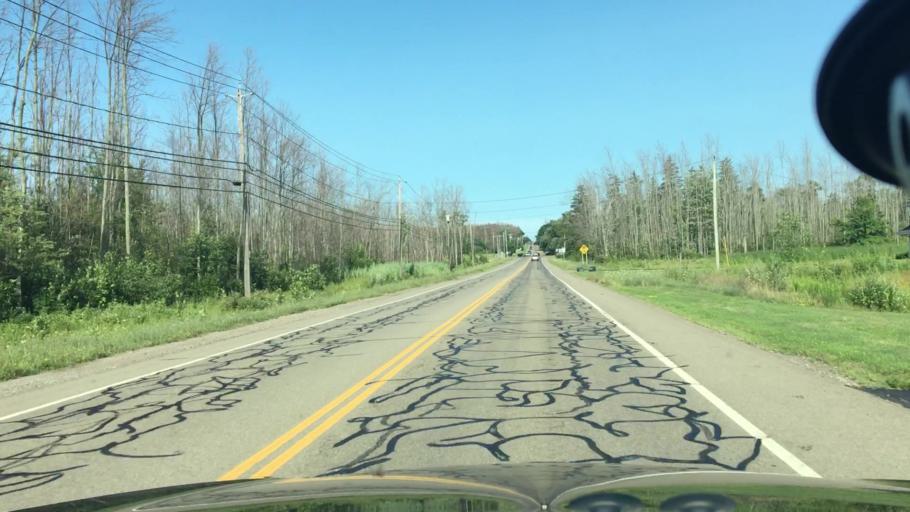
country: US
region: New York
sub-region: Erie County
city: Angola
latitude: 42.6525
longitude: -78.9861
